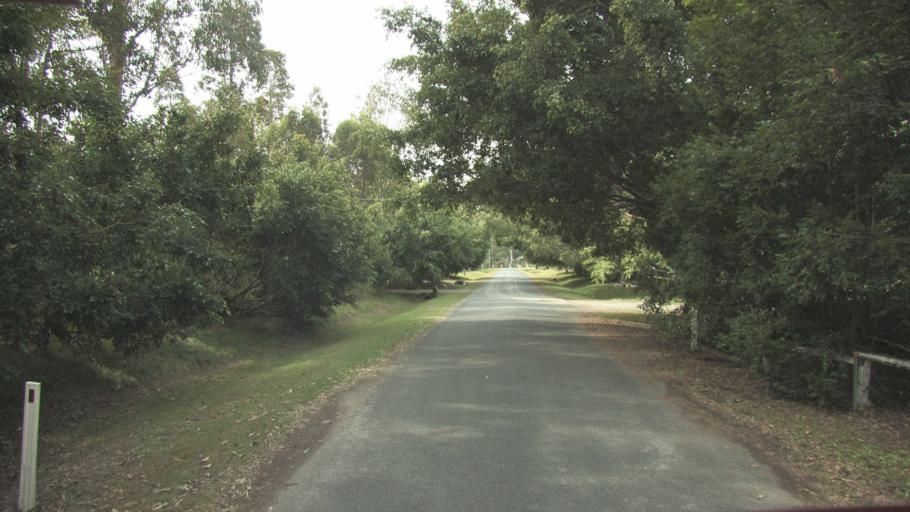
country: AU
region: Queensland
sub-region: Logan
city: Waterford West
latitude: -27.7334
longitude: 153.1356
